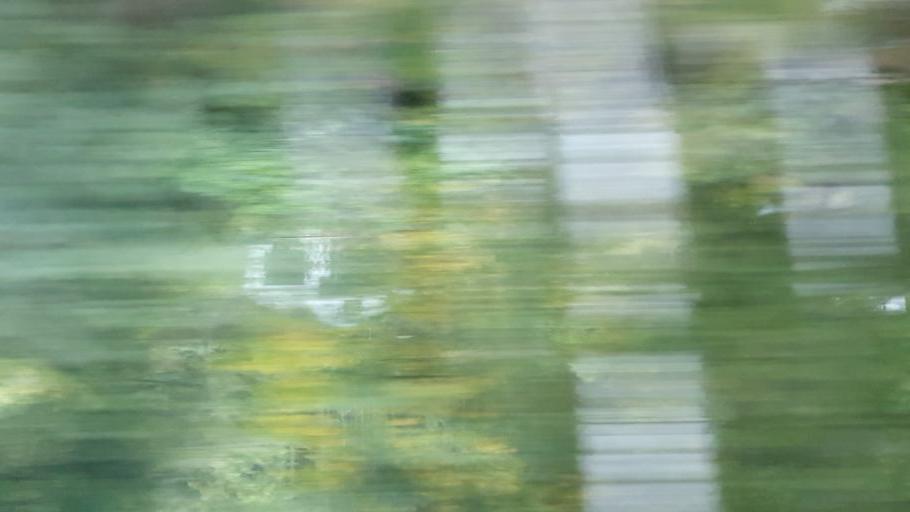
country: DE
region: Rheinland-Pfalz
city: Thaleischweiler-Froschen
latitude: 49.2626
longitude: 7.5908
